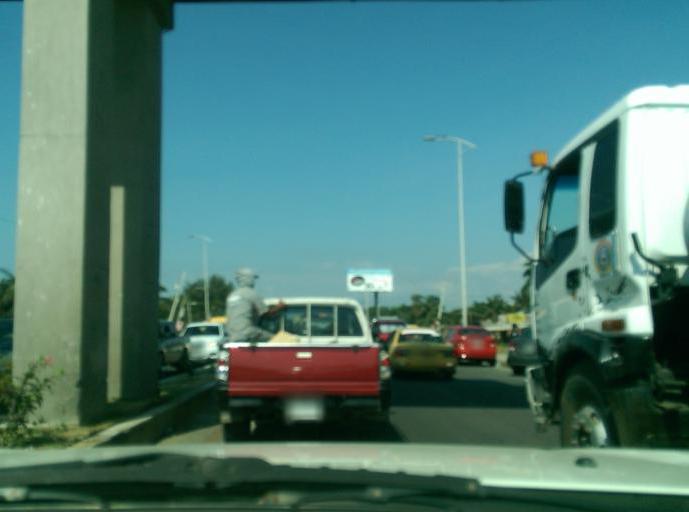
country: EC
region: Manabi
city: Manta
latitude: -0.9508
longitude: -80.7136
